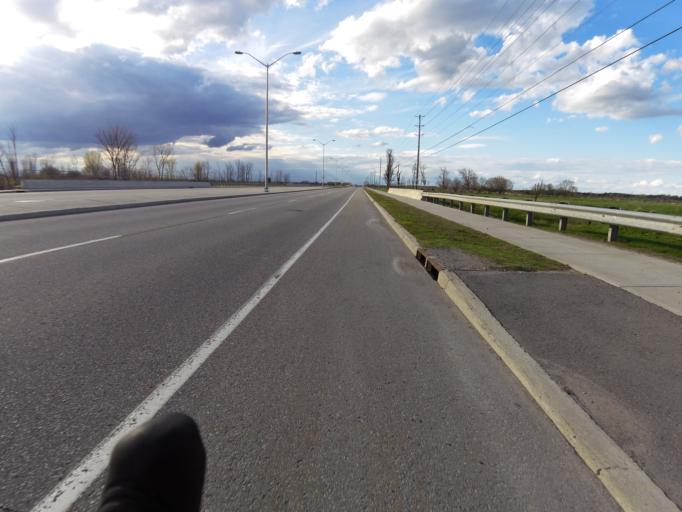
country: CA
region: Ontario
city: Ottawa
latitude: 45.2902
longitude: -75.6725
